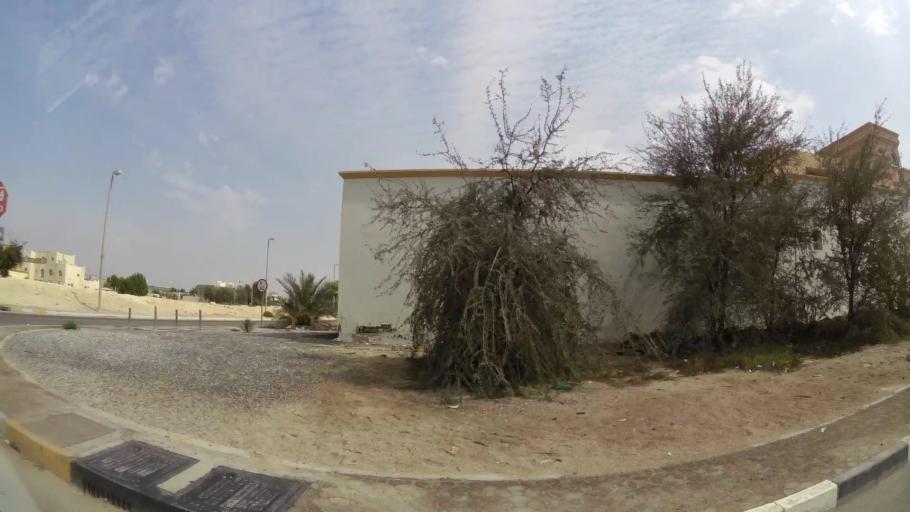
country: AE
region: Abu Dhabi
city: Abu Dhabi
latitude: 24.5268
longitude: 54.6822
